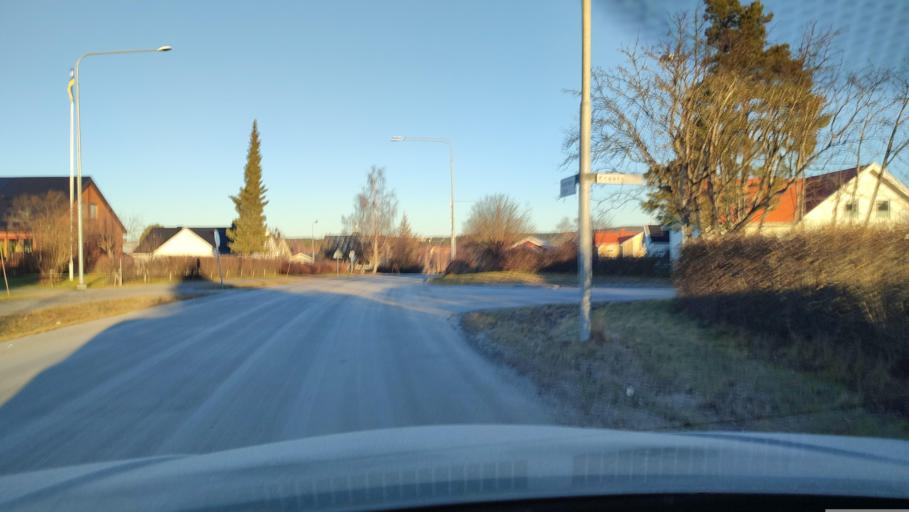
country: SE
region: Vaesterbotten
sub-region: Skelleftea Kommun
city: Viken
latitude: 64.7450
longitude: 20.9197
